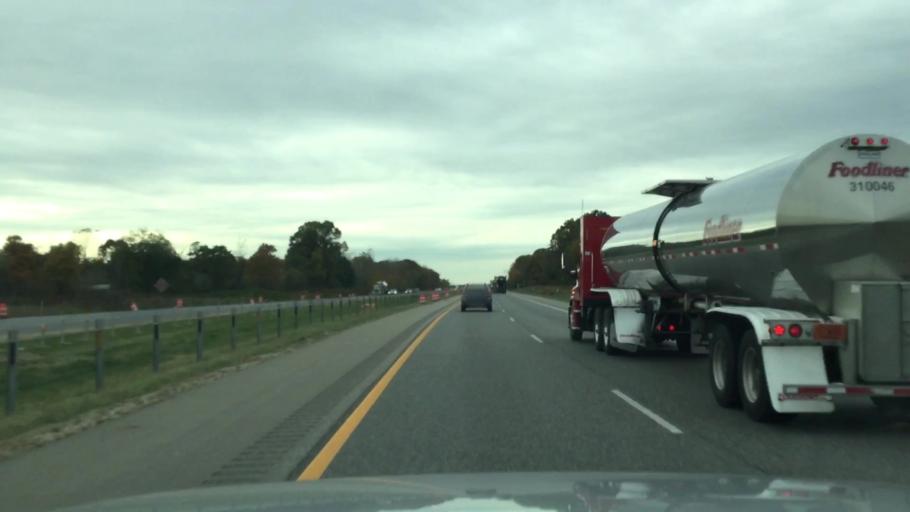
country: US
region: Michigan
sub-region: Van Buren County
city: Decatur
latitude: 42.1906
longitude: -86.0087
